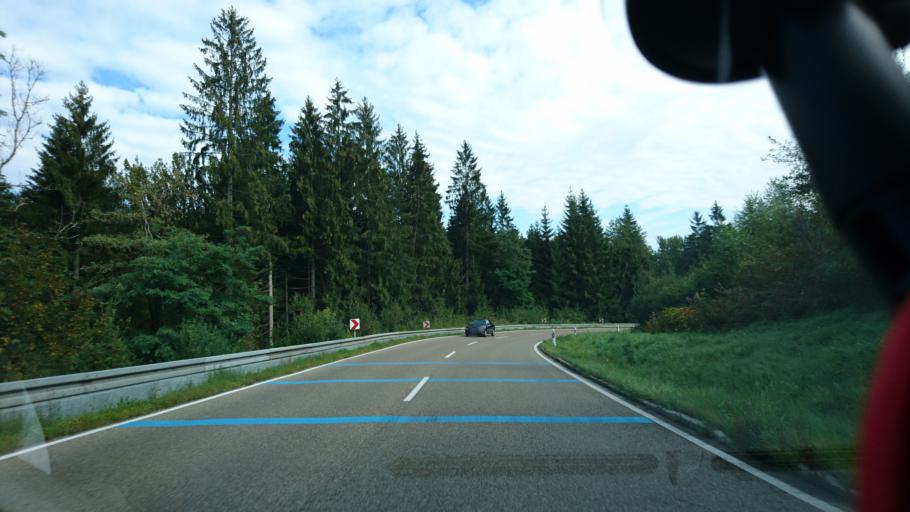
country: DE
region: Baden-Wuerttemberg
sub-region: Regierungsbezirk Stuttgart
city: Grosserlach
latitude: 49.0606
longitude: 9.5253
